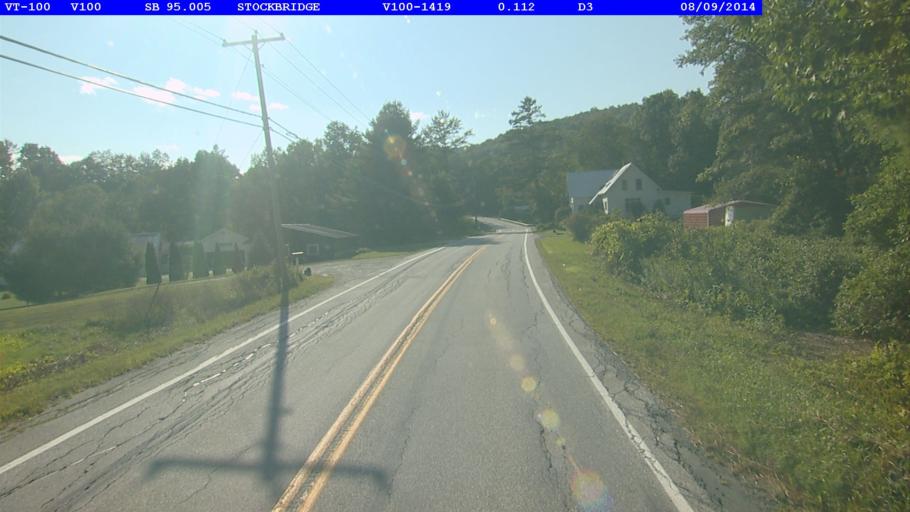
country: US
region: Vermont
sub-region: Orange County
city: Randolph
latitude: 43.7783
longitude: -72.7961
